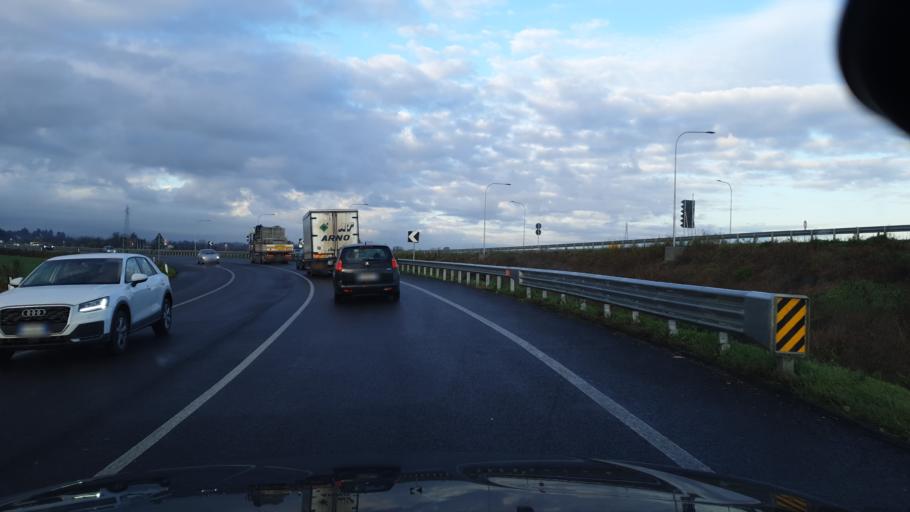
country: IT
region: Emilia-Romagna
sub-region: Provincia di Bologna
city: Crespellano
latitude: 44.5148
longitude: 11.1110
